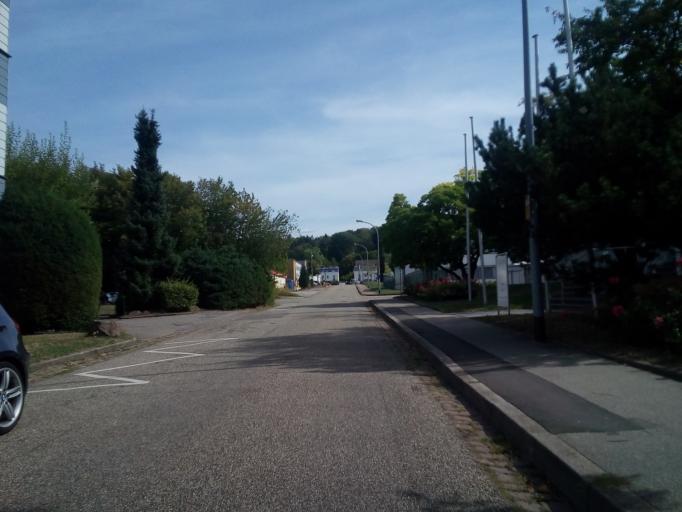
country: DE
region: Baden-Wuerttemberg
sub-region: Karlsruhe Region
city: Sinzheim
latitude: 48.7804
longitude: 8.1835
